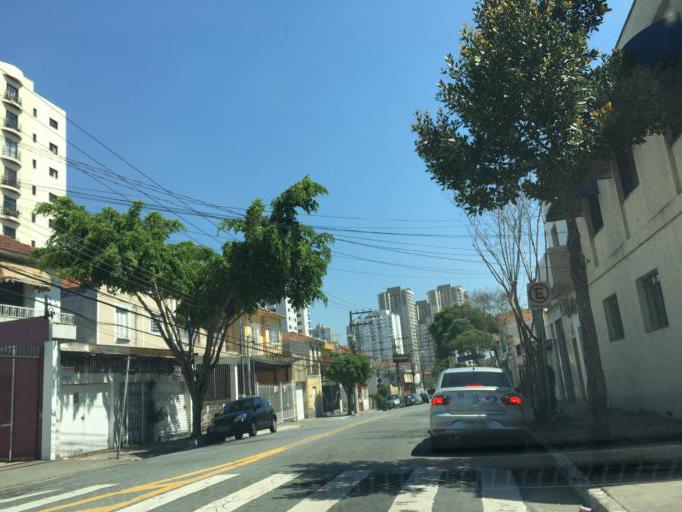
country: BR
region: Sao Paulo
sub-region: Sao Paulo
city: Sao Paulo
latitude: -23.5373
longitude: -46.5855
